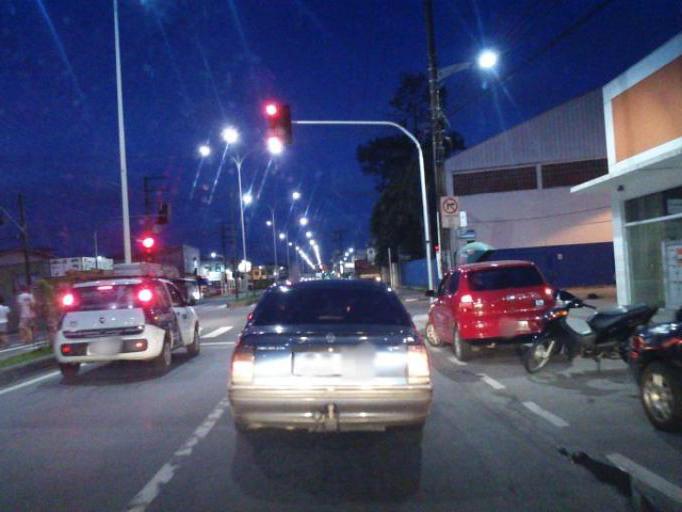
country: BR
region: Santa Catarina
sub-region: Itajai
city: Itajai
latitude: -26.8867
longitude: -48.6983
